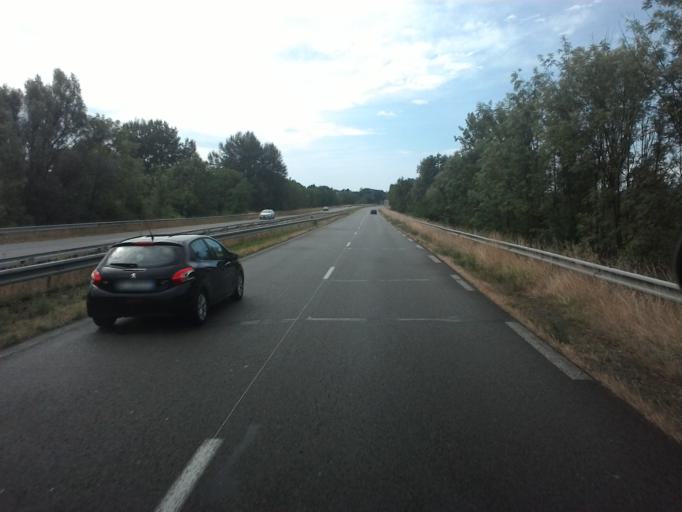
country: FR
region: Franche-Comte
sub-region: Departement du Jura
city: Montmorot
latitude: 46.7647
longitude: 5.5553
